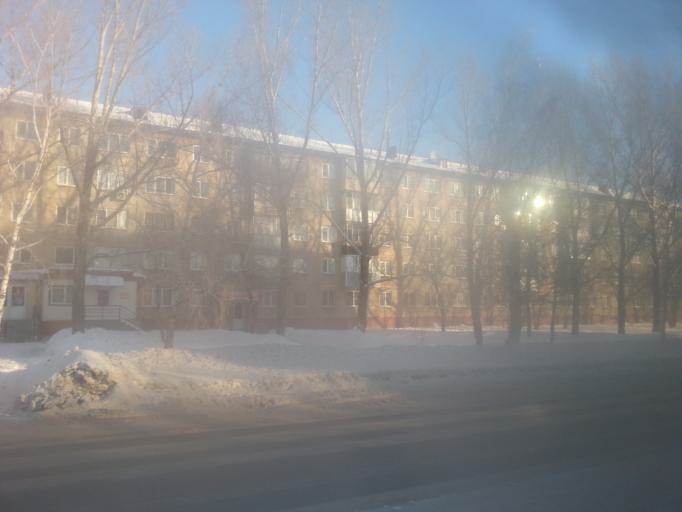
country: RU
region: Altai Krai
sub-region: Gorod Barnaulskiy
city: Barnaul
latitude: 53.3584
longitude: 83.7055
